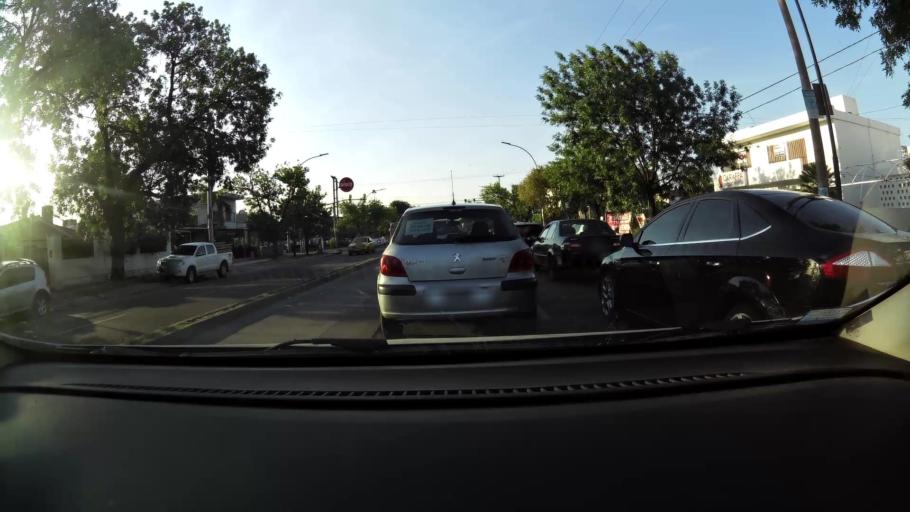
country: AR
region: Cordoba
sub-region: Departamento de Capital
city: Cordoba
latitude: -31.3775
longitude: -64.2253
